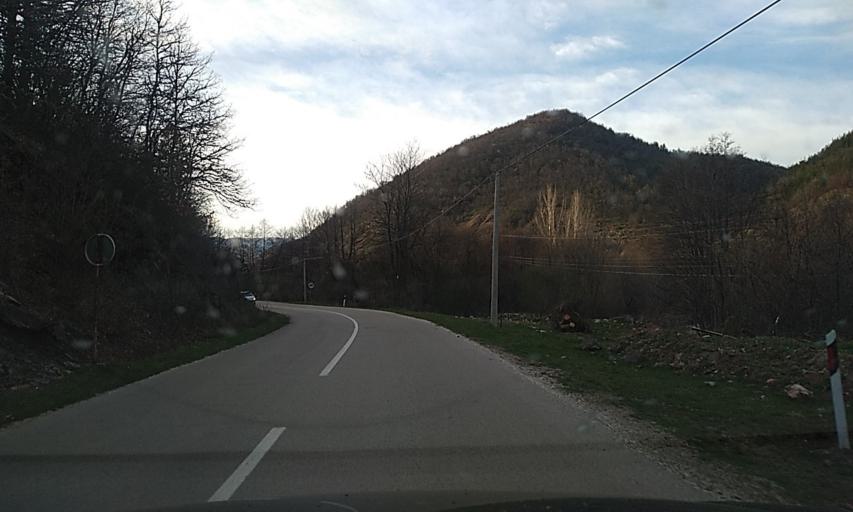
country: RS
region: Central Serbia
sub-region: Pcinjski Okrug
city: Bosilegrad
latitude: 42.4505
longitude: 22.5007
